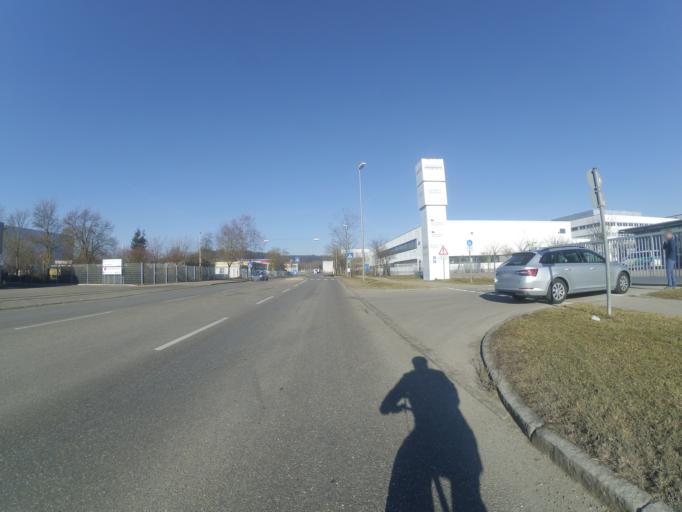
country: DE
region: Baden-Wuerttemberg
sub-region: Tuebingen Region
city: Erbach
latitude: 48.3598
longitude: 9.9391
